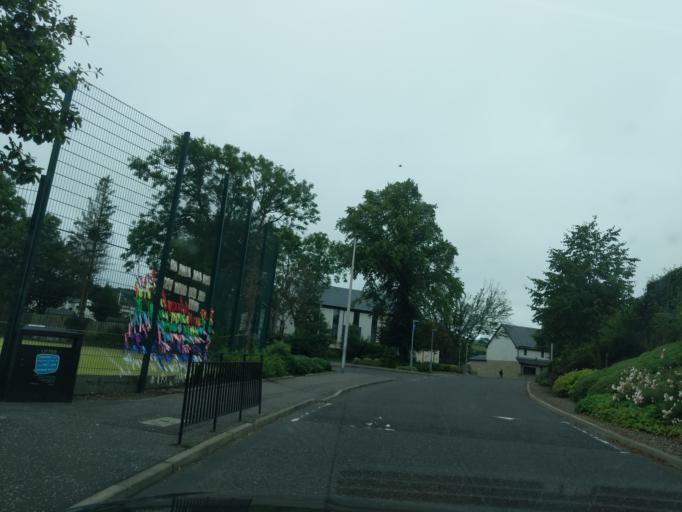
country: GB
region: Scotland
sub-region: Edinburgh
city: Currie
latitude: 55.9061
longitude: -3.2867
